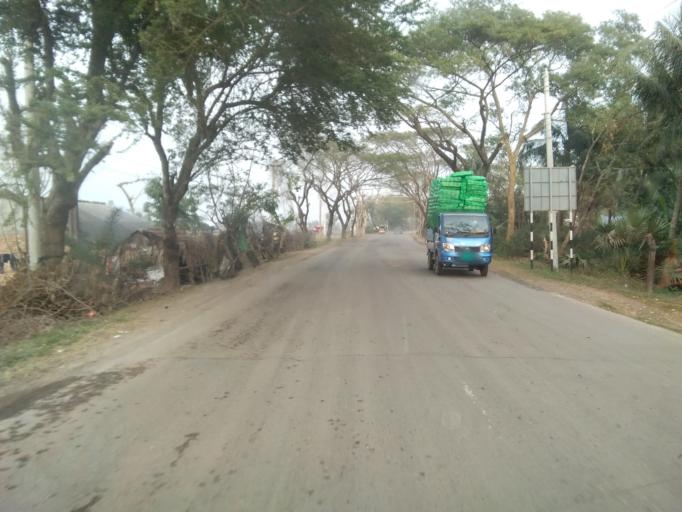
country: BD
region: Khulna
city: Satkhira
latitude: 22.6892
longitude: 89.0338
